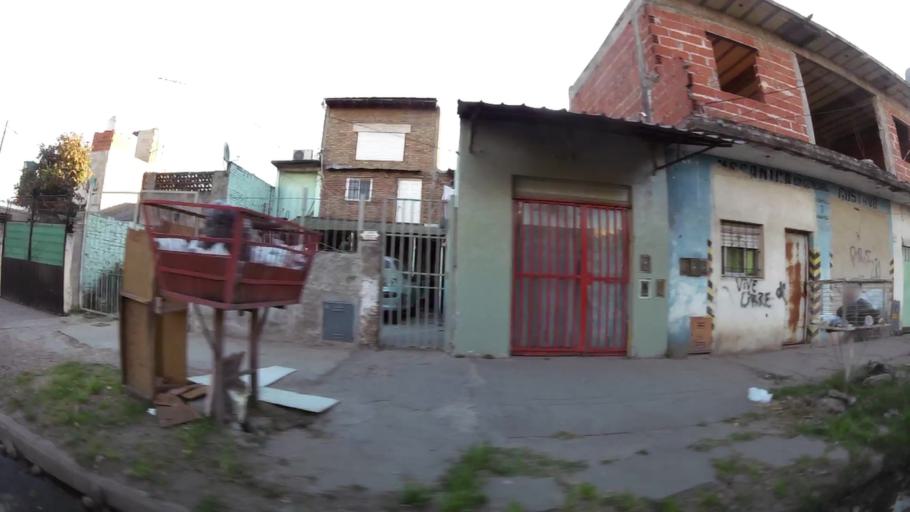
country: AR
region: Buenos Aires
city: San Justo
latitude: -34.7316
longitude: -58.6096
